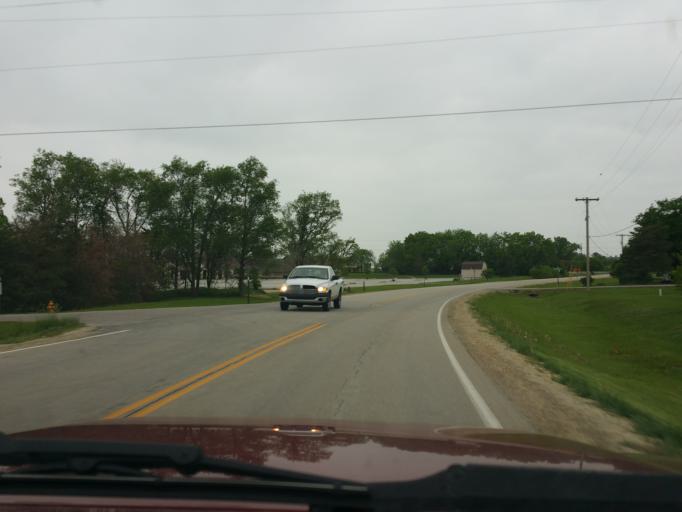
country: US
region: Kansas
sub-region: Riley County
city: Manhattan
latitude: 39.2299
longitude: -96.5804
